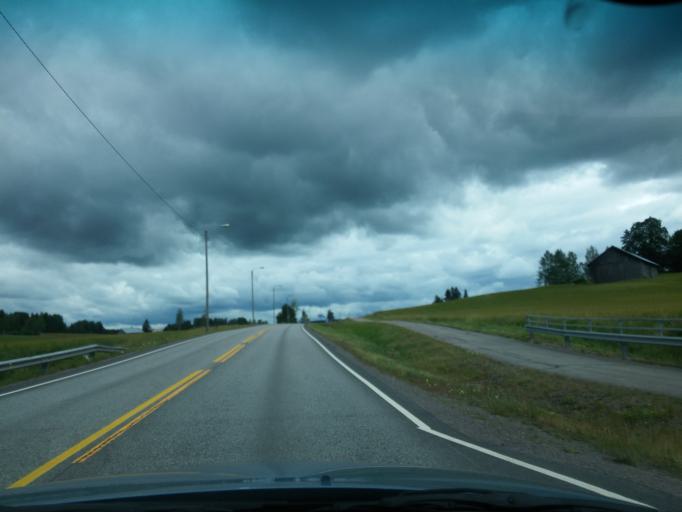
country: FI
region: Uusimaa
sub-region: Porvoo
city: Askola
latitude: 60.5182
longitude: 25.5792
